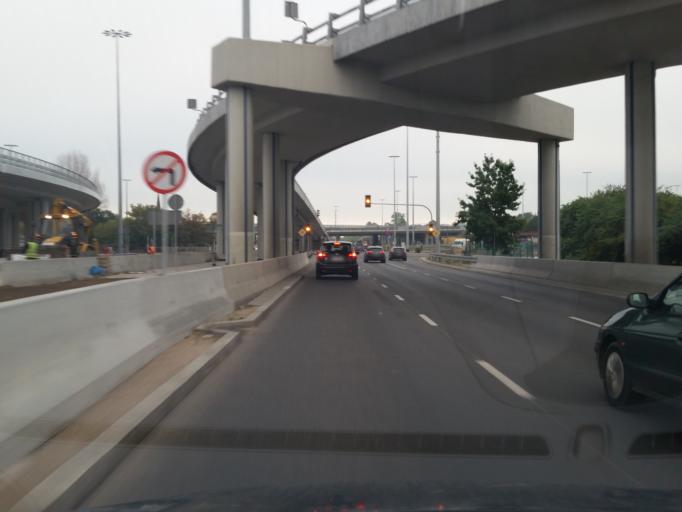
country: PL
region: Masovian Voivodeship
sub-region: Warszawa
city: Zoliborz
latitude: 52.2927
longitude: 21.0005
